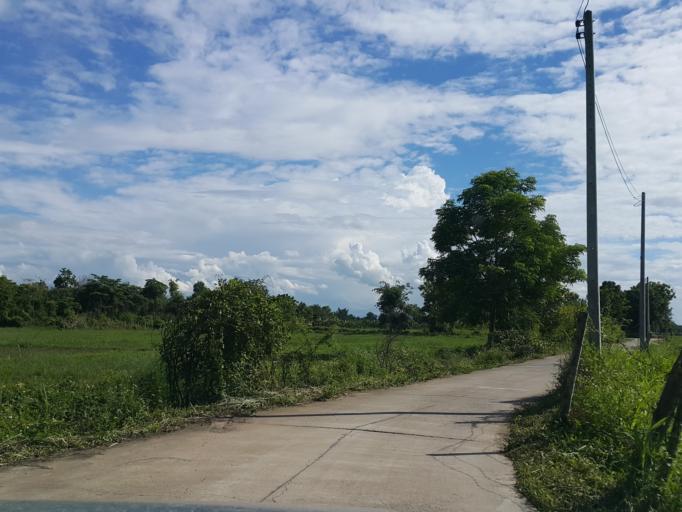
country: TH
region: Chiang Mai
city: San Kamphaeng
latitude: 18.7896
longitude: 99.1221
